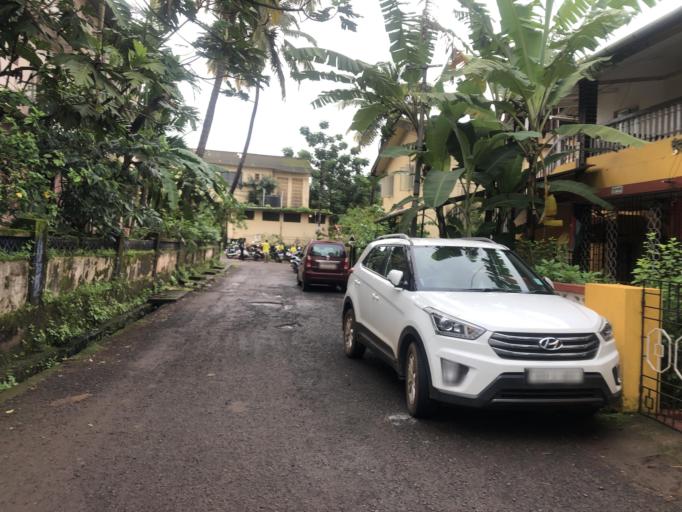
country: IN
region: Goa
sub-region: North Goa
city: Mapuca
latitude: 15.5952
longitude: 73.8044
